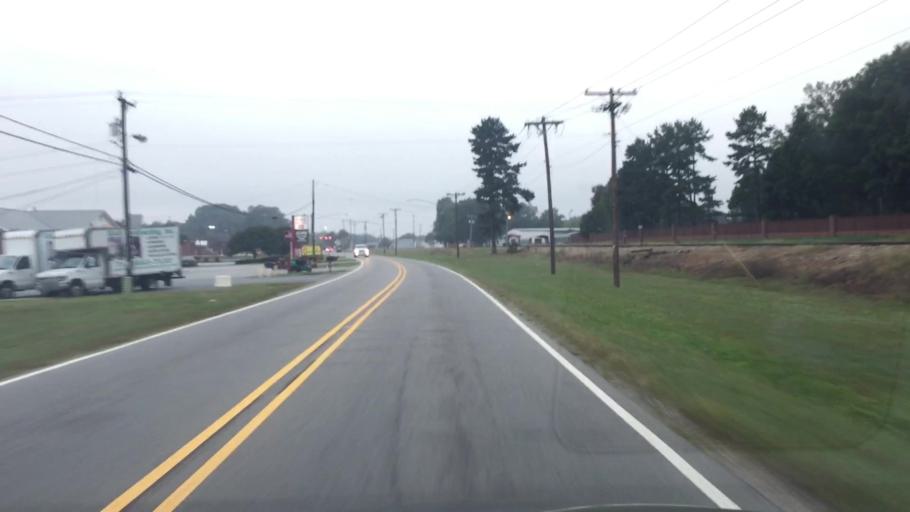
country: US
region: North Carolina
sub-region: Iredell County
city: Mooresville
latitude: 35.5978
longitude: -80.8089
